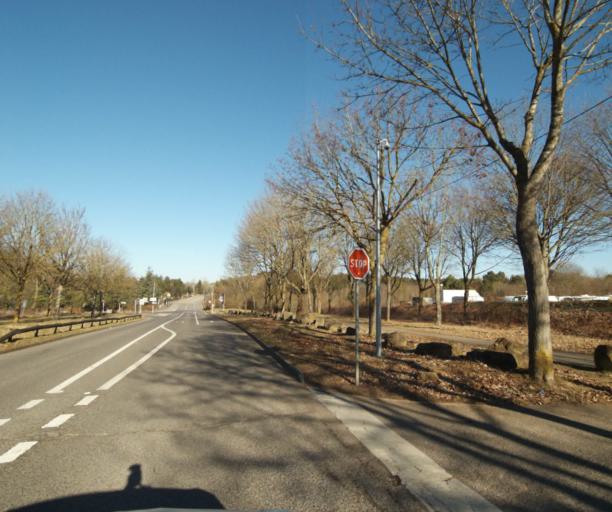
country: FR
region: Lorraine
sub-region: Departement de Meurthe-et-Moselle
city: Maxeville
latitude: 48.7097
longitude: 6.1484
